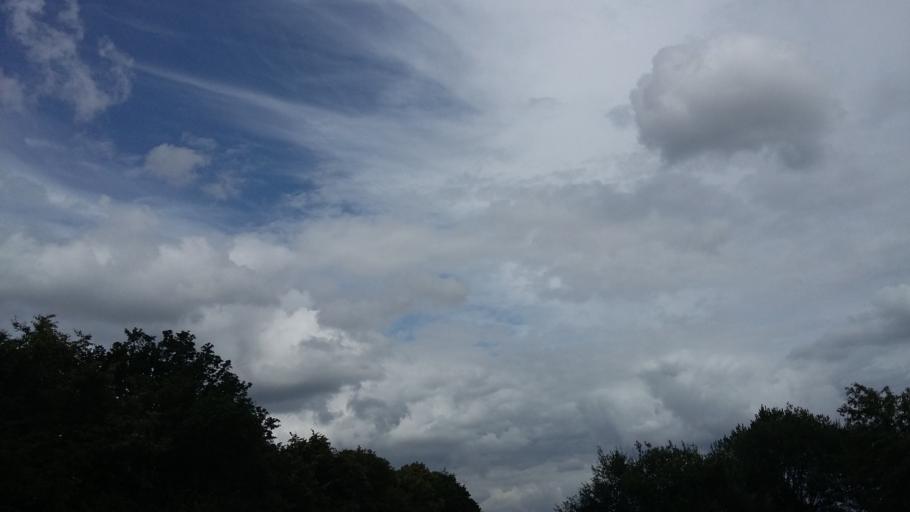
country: DE
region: Lower Saxony
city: Laatzen
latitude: 52.3022
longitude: 9.8293
